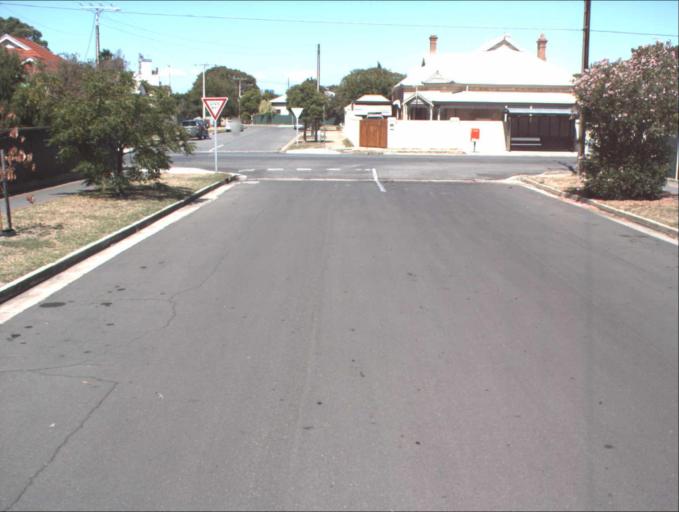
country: AU
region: South Australia
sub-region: Port Adelaide Enfield
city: Birkenhead
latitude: -34.8288
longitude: 138.4878
